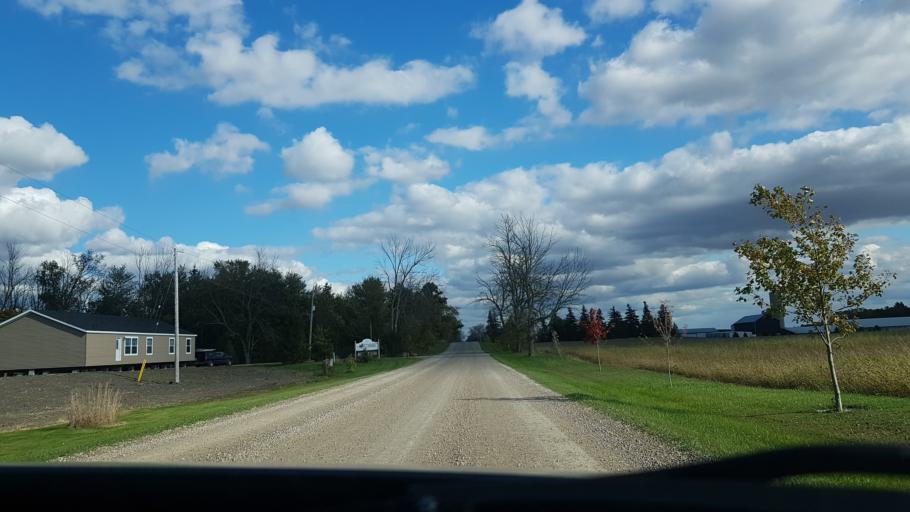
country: CA
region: Ontario
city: South Huron
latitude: 43.1114
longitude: -81.6399
